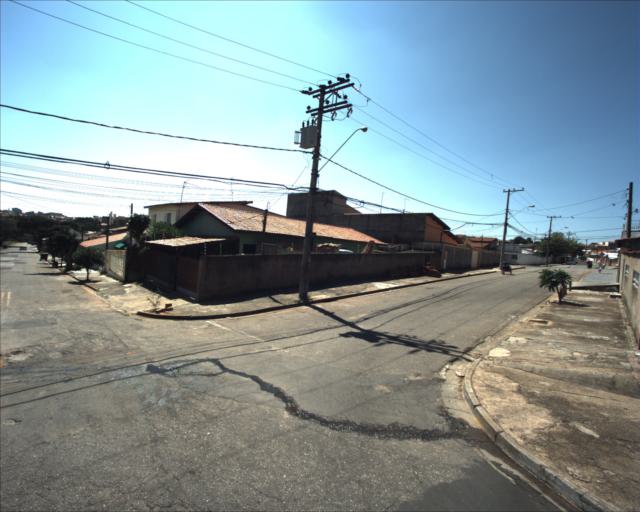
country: BR
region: Sao Paulo
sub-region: Sorocaba
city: Sorocaba
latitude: -23.4721
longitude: -47.4806
